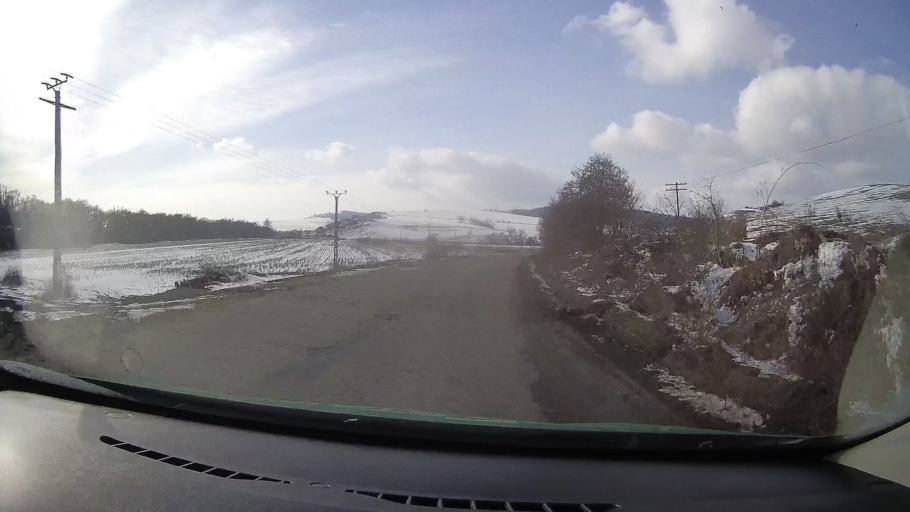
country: RO
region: Sibiu
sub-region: Comuna Iacobeni
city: Iacobeni
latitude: 46.0434
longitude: 24.7521
